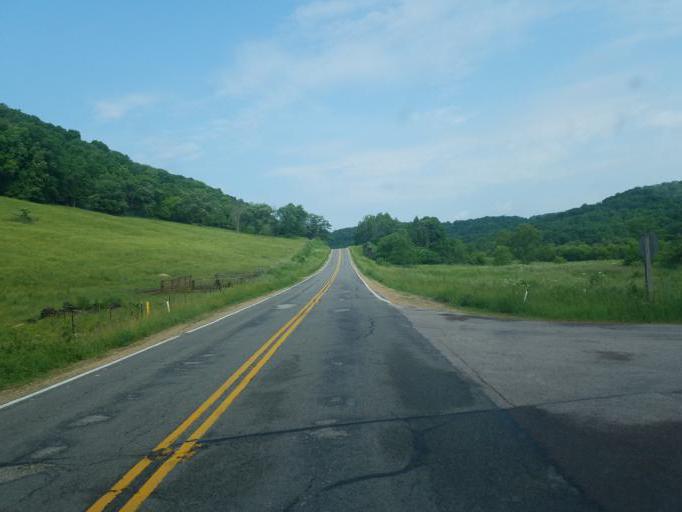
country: US
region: Wisconsin
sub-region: Vernon County
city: Hillsboro
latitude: 43.6755
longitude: -90.4994
